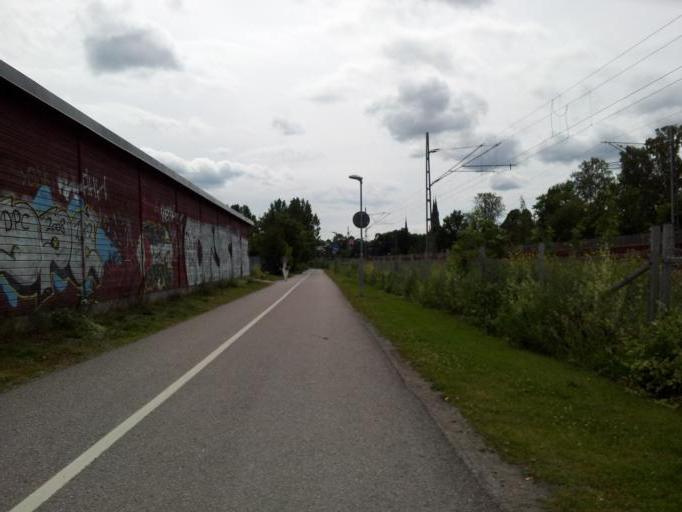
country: SE
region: Uppsala
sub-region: Uppsala Kommun
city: Uppsala
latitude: 59.8677
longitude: 17.6360
